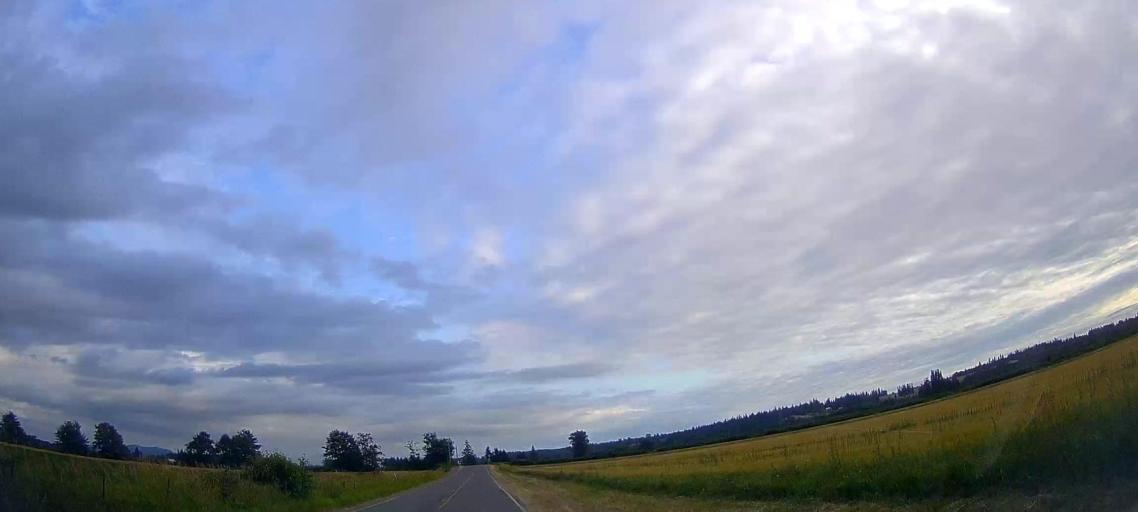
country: US
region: Washington
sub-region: Skagit County
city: Burlington
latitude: 48.5227
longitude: -122.4113
